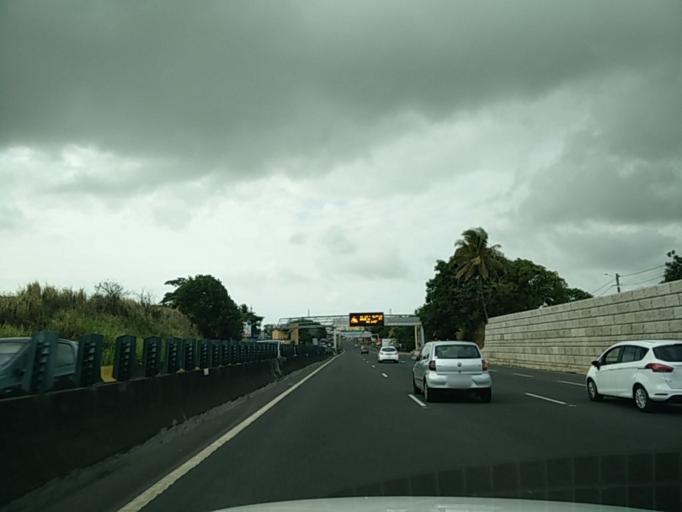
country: GP
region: Guadeloupe
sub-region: Guadeloupe
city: Baie-Mahault
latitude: 16.2333
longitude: -61.5902
